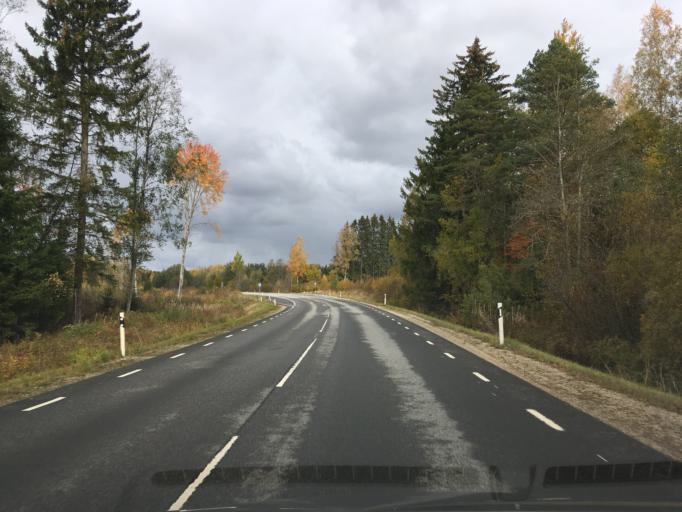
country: EE
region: Harju
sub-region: Anija vald
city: Kehra
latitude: 59.2915
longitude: 25.3758
